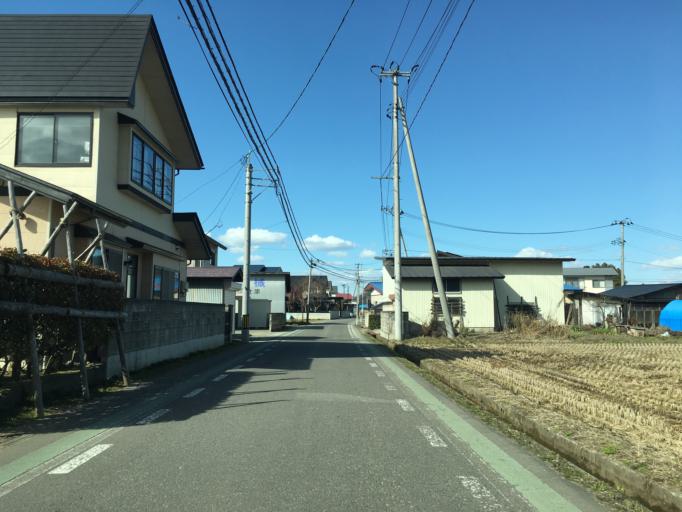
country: JP
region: Yamagata
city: Yonezawa
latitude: 37.9278
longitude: 140.1435
